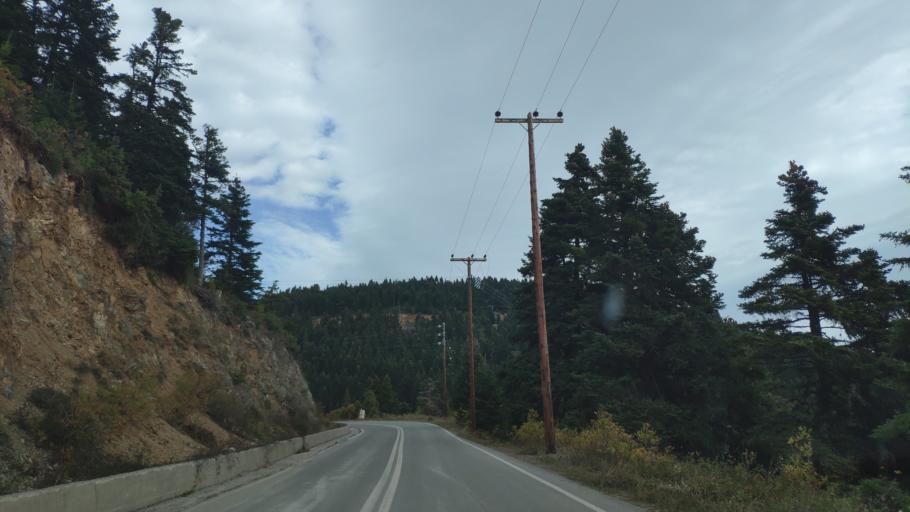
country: GR
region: Central Greece
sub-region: Nomos Fokidos
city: Amfissa
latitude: 38.6988
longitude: 22.3168
